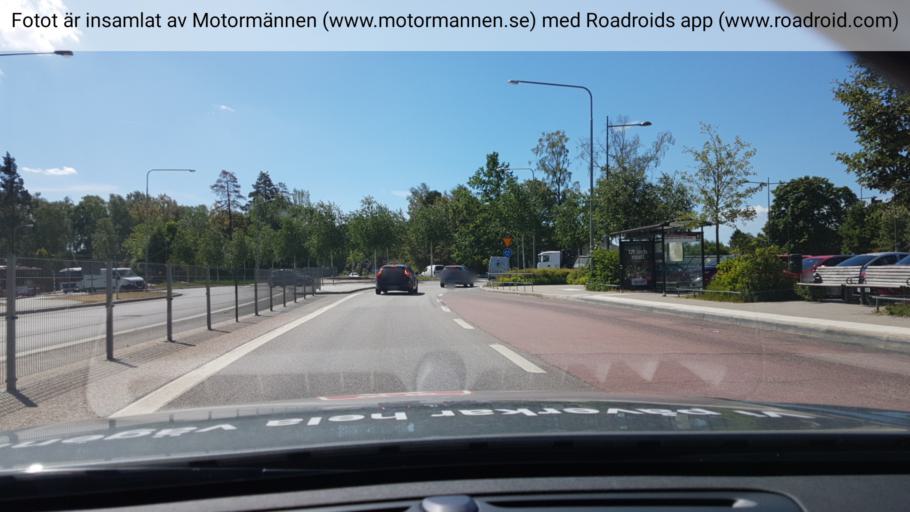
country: SE
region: Stockholm
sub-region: Tyreso Kommun
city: Bollmora
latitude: 59.2238
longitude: 18.2023
